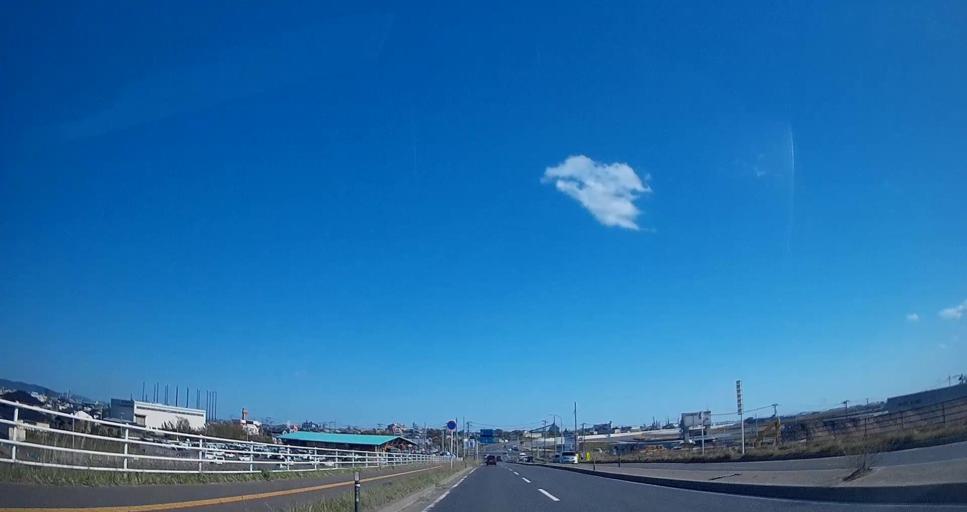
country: JP
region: Miyagi
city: Yamoto
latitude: 38.4326
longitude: 141.2481
